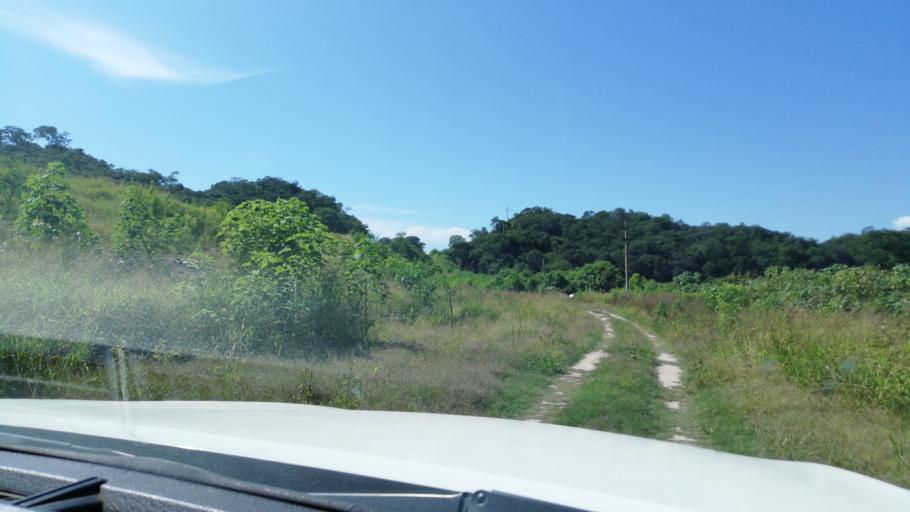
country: AR
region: Jujuy
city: La Mendieta
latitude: -24.3795
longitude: -65.0495
